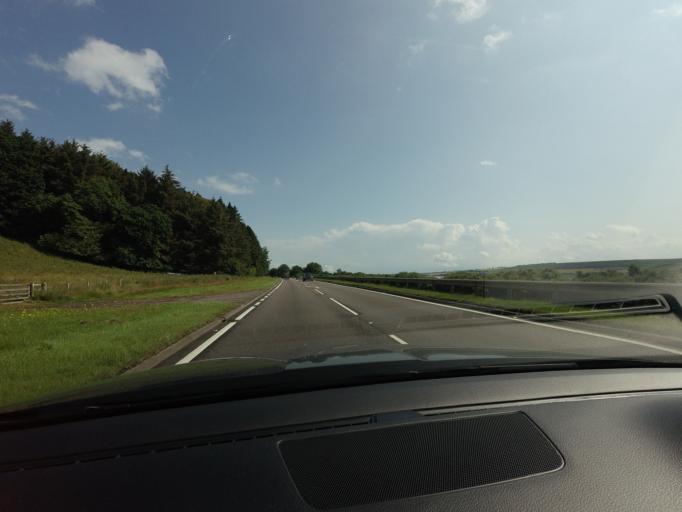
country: GB
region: Scotland
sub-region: Highland
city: Evanton
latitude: 57.6379
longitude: -4.3538
